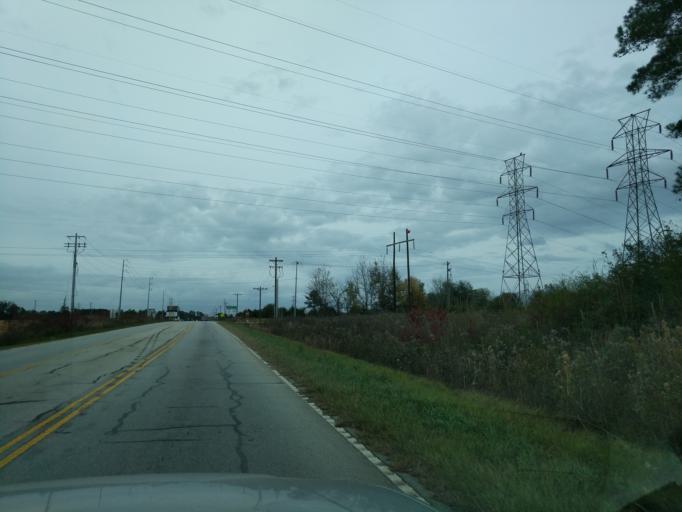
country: US
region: South Carolina
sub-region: Newberry County
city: Newberry
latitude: 34.2605
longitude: -81.6392
